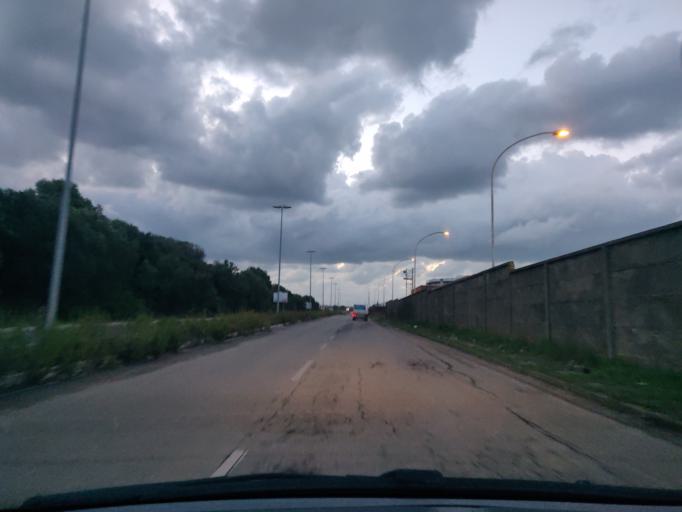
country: IT
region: Latium
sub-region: Citta metropolitana di Roma Capitale
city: Civitavecchia
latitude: 42.1127
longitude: 11.7812
